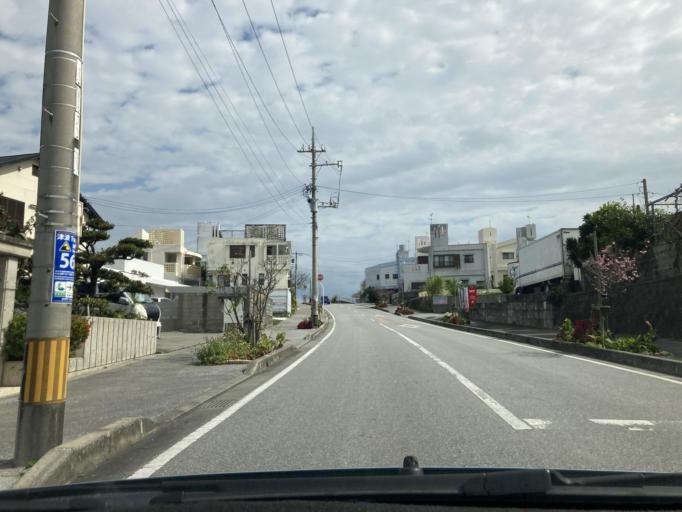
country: JP
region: Okinawa
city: Tomigusuku
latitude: 26.1858
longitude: 127.6930
